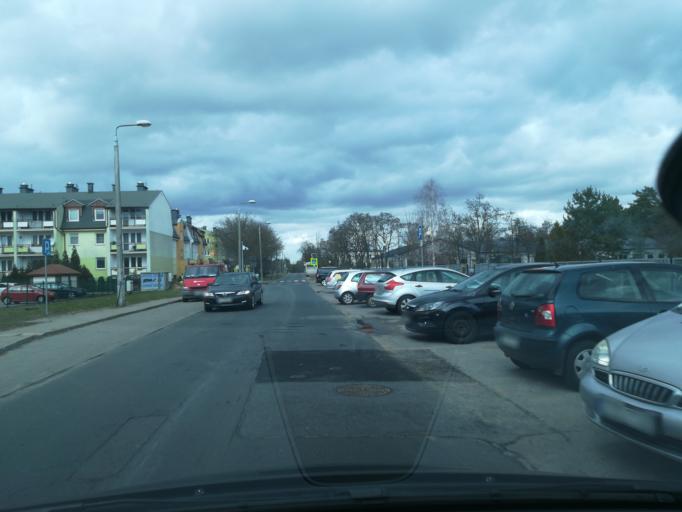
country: PL
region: Kujawsko-Pomorskie
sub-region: Powiat torunski
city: Lubicz Dolny
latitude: 52.9805
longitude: 18.6852
